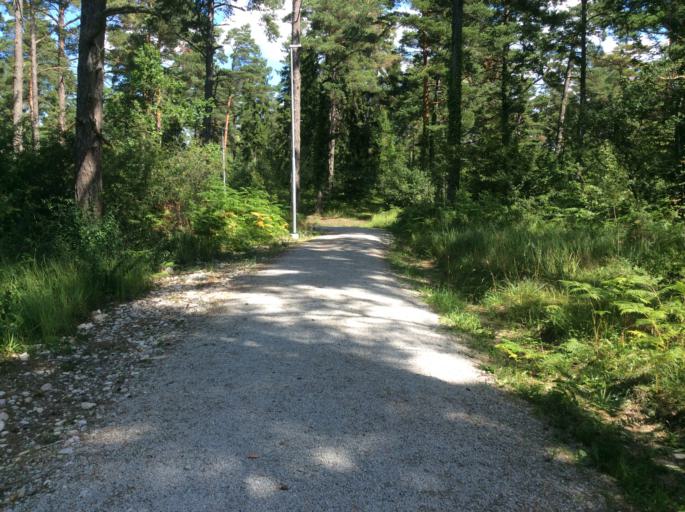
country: SE
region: Gotland
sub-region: Gotland
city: Vibble
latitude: 57.6018
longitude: 18.2755
